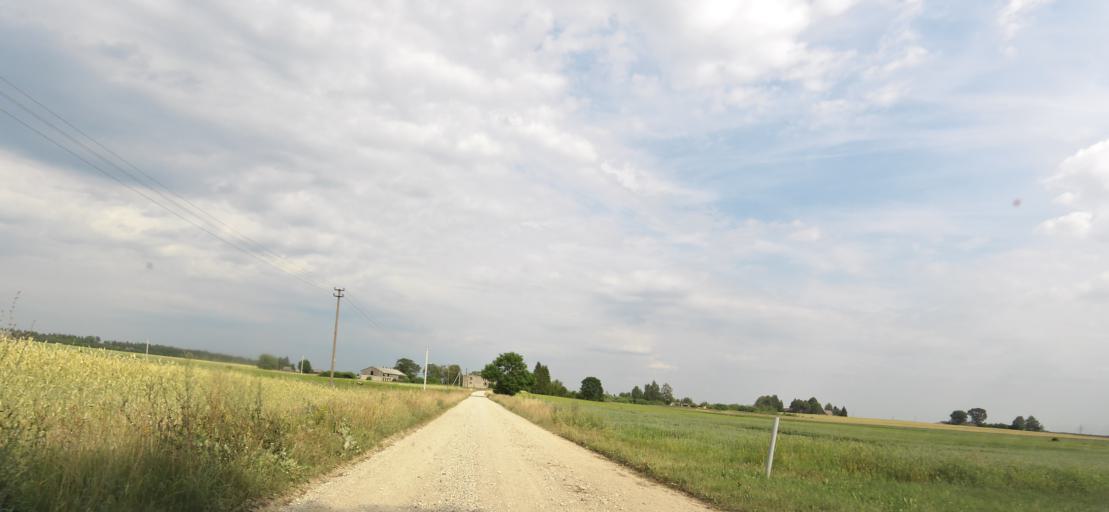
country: LT
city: Obeliai
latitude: 56.1556
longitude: 25.0004
